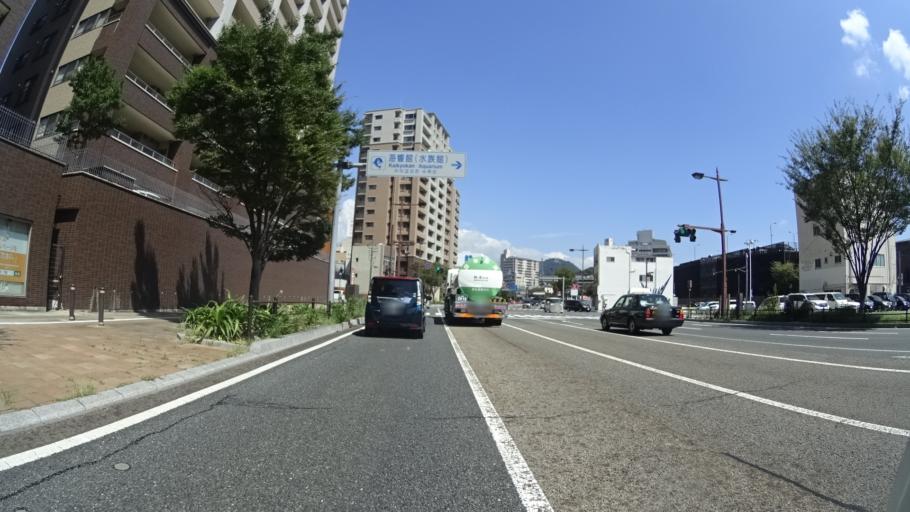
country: JP
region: Yamaguchi
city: Shimonoseki
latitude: 33.9548
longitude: 130.9405
